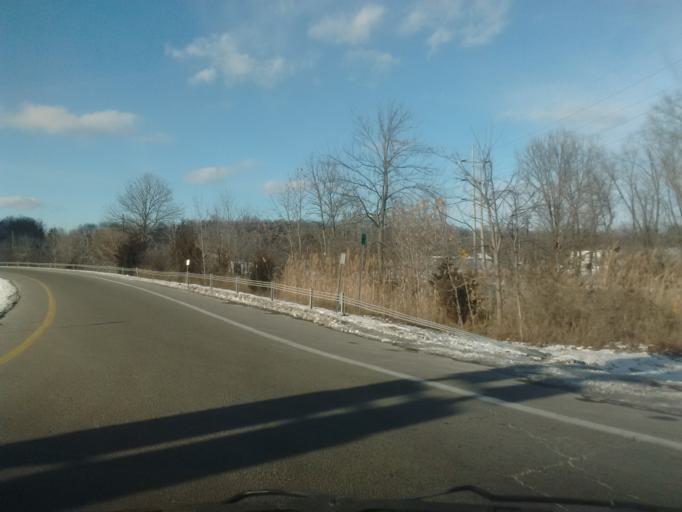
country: US
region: New York
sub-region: Dutchess County
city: Fishkill
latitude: 41.5276
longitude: -73.9159
